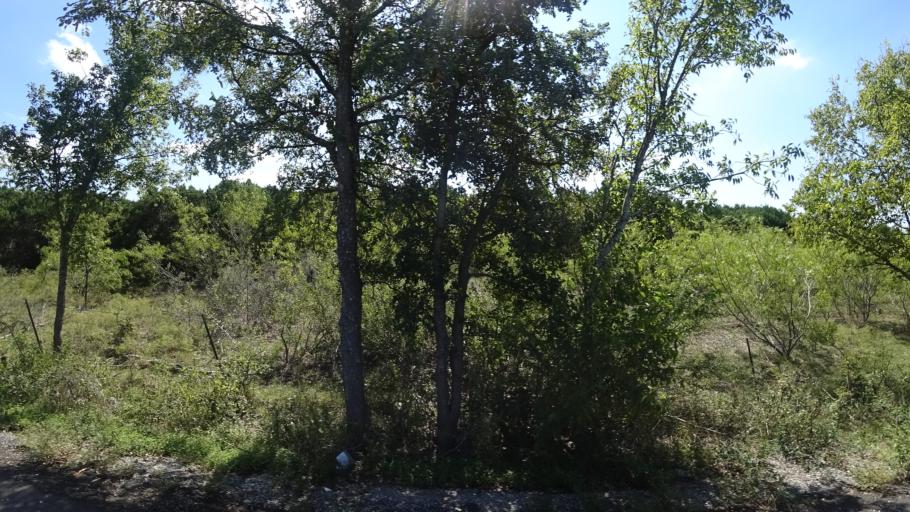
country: US
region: Texas
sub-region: Travis County
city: Manor
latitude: 30.3525
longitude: -97.6383
